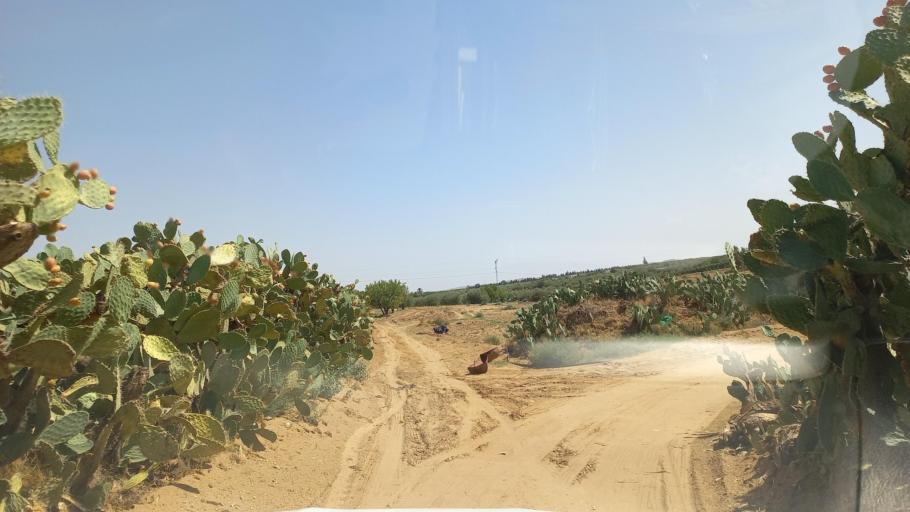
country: TN
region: Al Qasrayn
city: Kasserine
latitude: 35.2375
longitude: 9.0314
